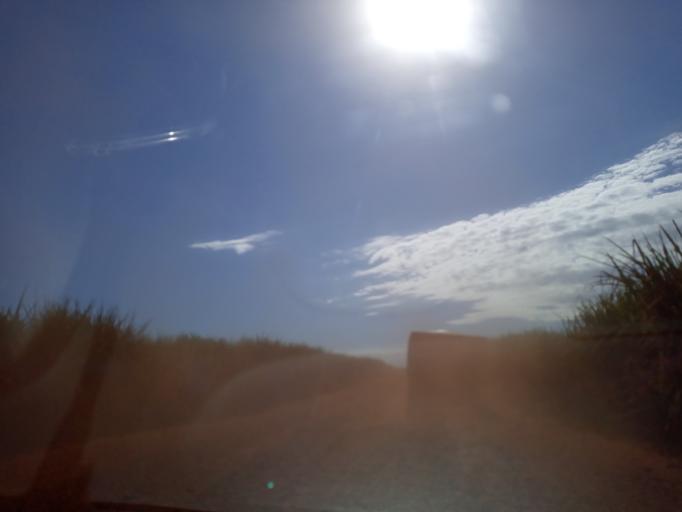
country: BR
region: Goias
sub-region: Itumbiara
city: Itumbiara
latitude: -18.4506
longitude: -49.1824
